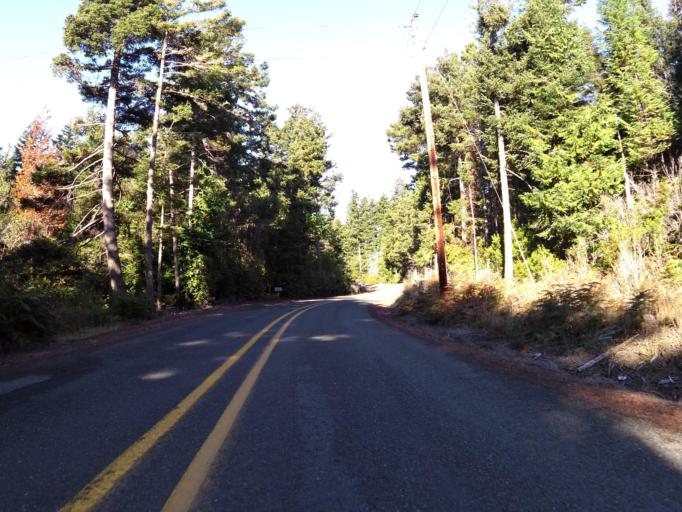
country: US
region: Oregon
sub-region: Coos County
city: Bandon
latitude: 43.0389
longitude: -124.3980
